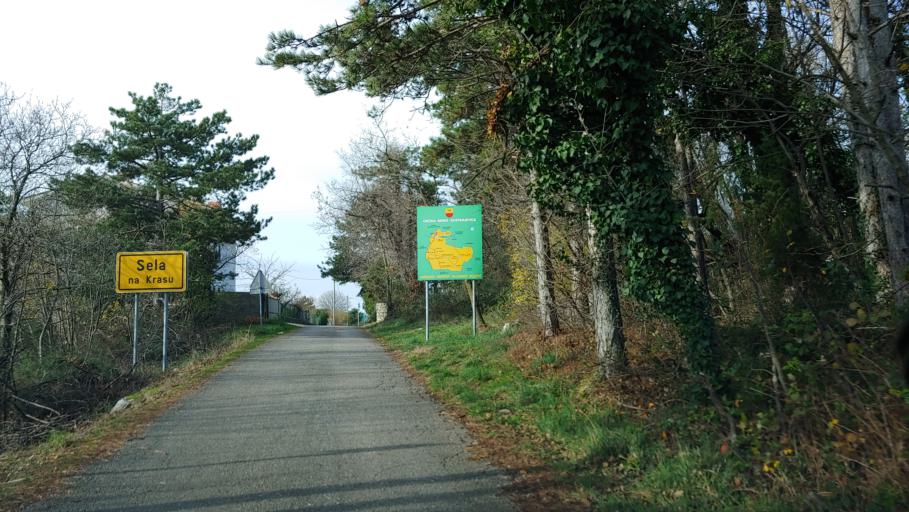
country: IT
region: Friuli Venezia Giulia
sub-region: Provincia di Trieste
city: Duino
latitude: 45.8194
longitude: 13.6186
